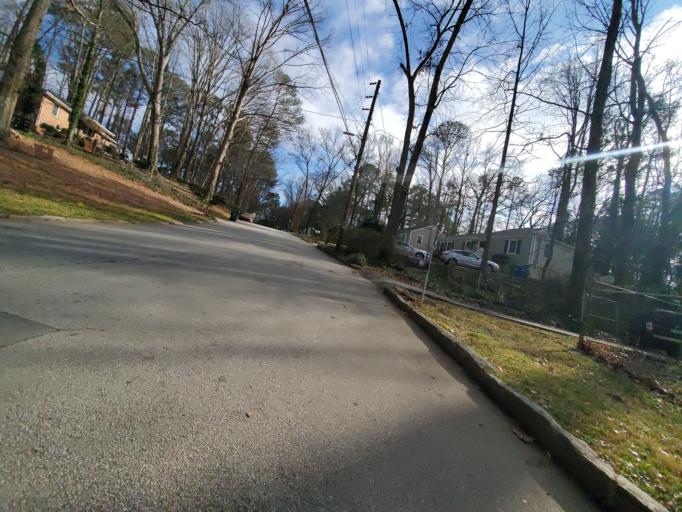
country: US
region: Georgia
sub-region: DeKalb County
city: North Decatur
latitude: 33.8030
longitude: -84.2923
